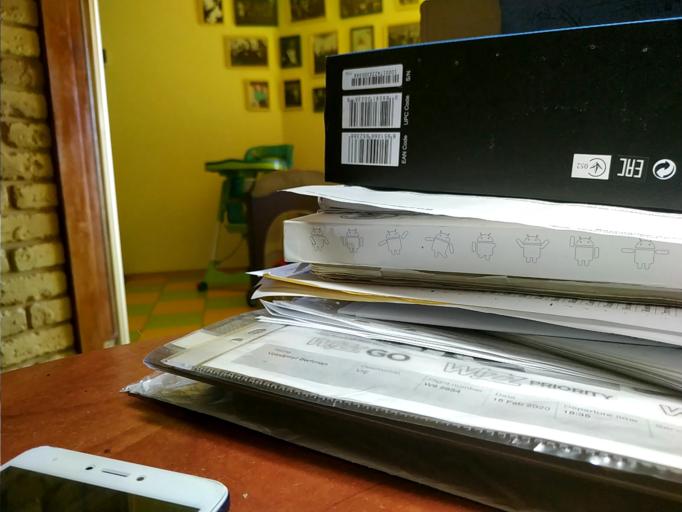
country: RU
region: Novgorod
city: Kholm
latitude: 59.2451
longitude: 32.8726
